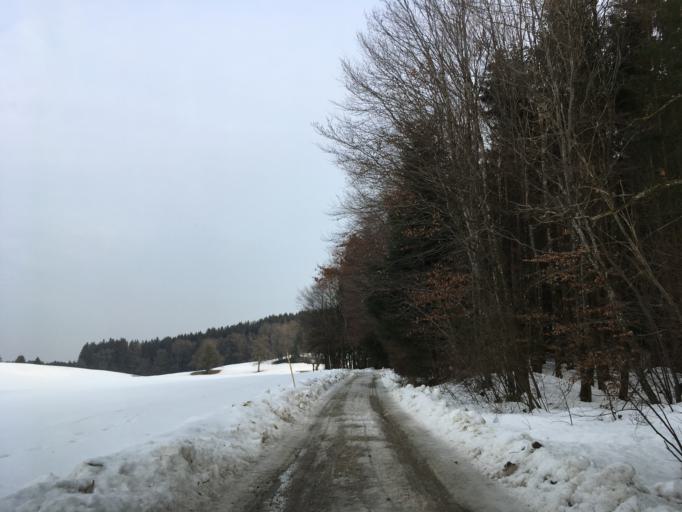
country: DE
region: Bavaria
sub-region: Upper Bavaria
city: Bad Endorf
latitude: 47.9256
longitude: 12.3089
